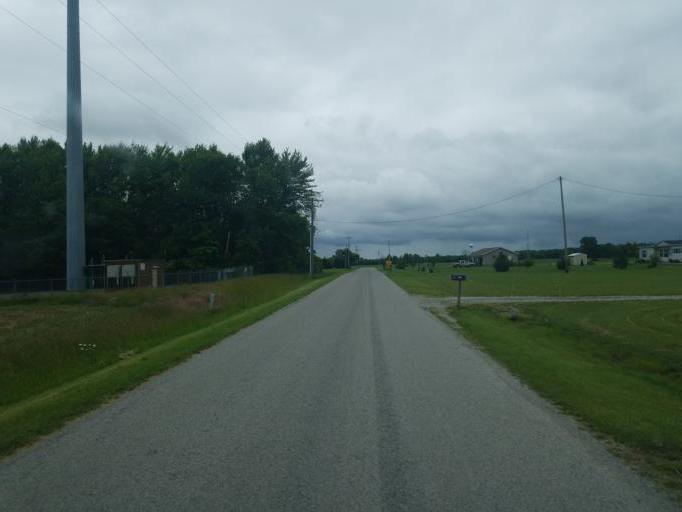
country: US
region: Ohio
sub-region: Morrow County
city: Cardington
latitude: 40.5399
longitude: -82.8767
